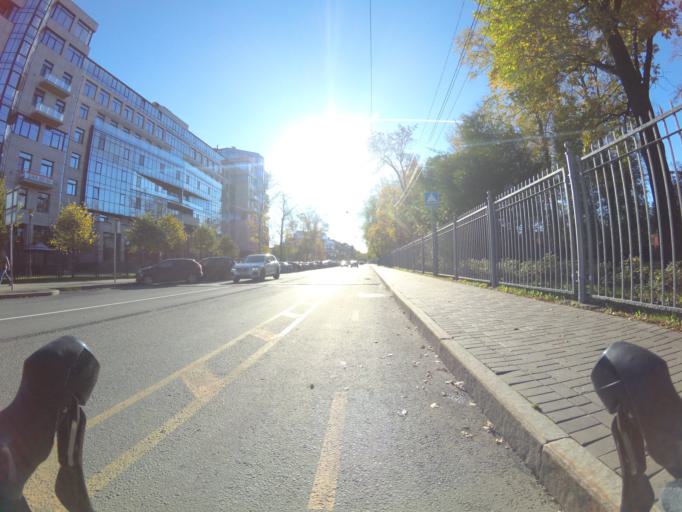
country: RU
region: Leningrad
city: Krestovskiy ostrov
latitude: 59.9734
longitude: 30.2583
